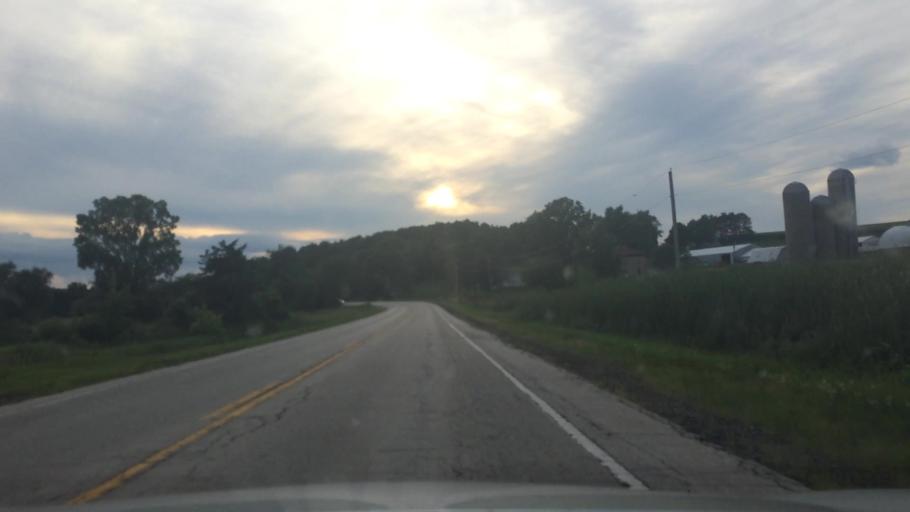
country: US
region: Wisconsin
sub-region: Columbia County
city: Lodi
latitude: 43.3196
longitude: -89.5126
